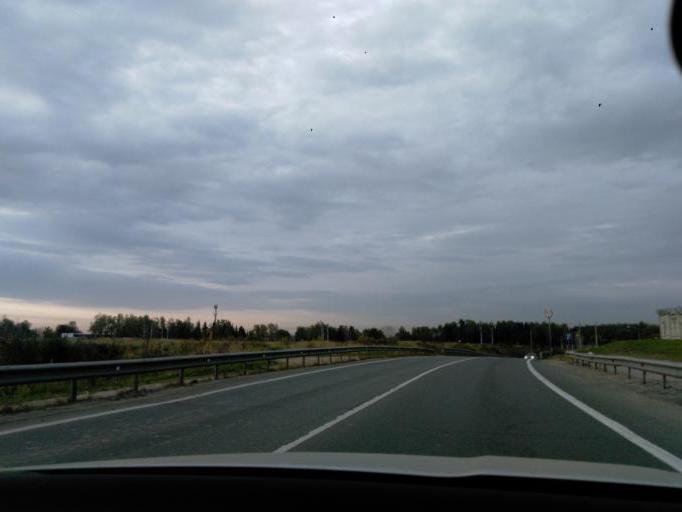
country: RU
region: Moskovskaya
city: Sheremet'yevskiy
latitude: 55.9772
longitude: 37.4541
